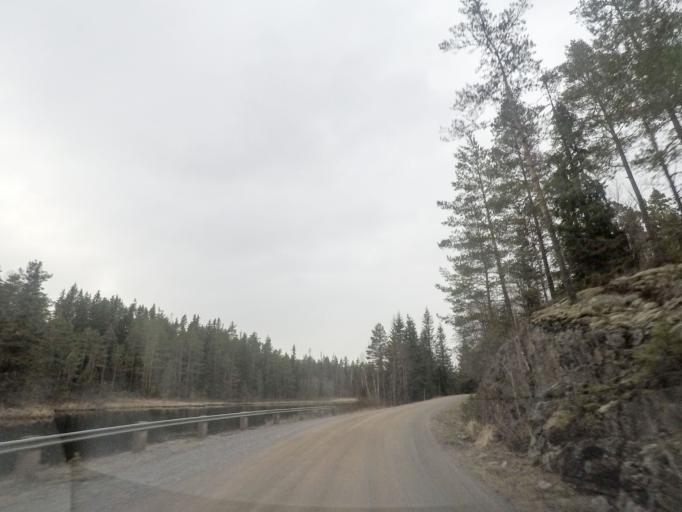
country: SE
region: Dalarna
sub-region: Ludvika Kommun
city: Abborrberget
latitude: 60.0208
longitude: 14.6087
